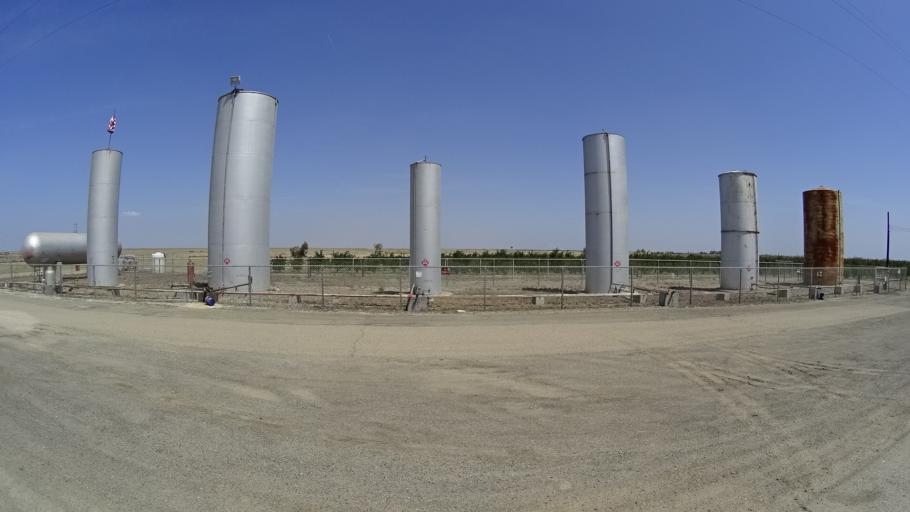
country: US
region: California
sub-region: Kings County
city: Stratford
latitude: 36.1233
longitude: -119.8905
